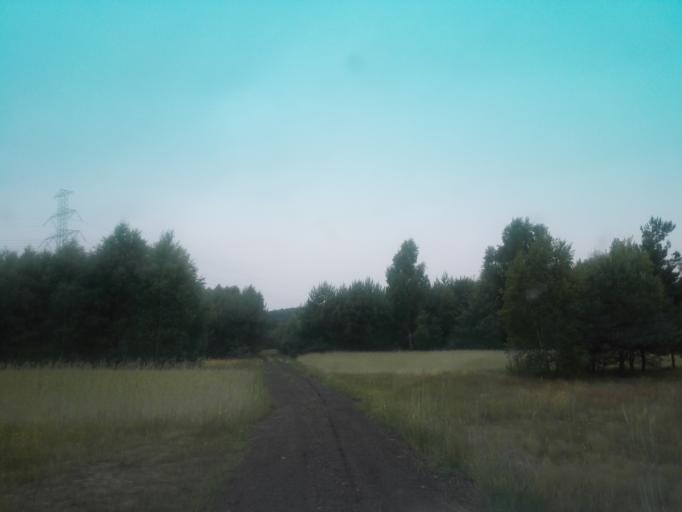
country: PL
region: Silesian Voivodeship
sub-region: Powiat czestochowski
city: Olsztyn
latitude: 50.7900
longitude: 19.2625
